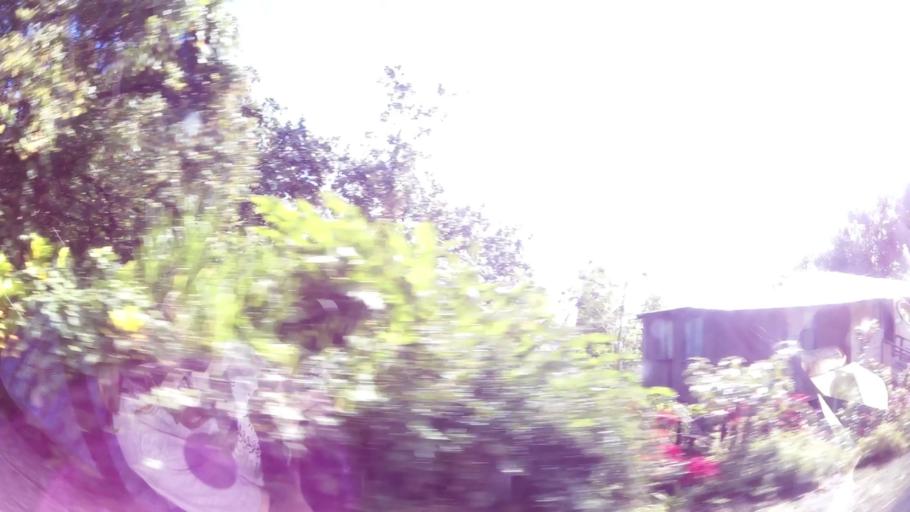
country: DM
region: Saint Andrew
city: Marigot
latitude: 15.5124
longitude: -61.2629
